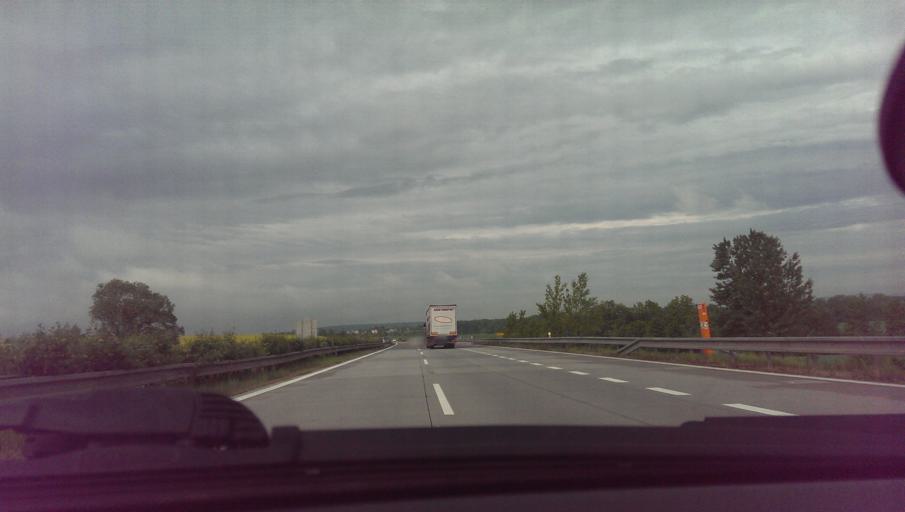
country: CZ
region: South Moravian
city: Ivanovice na Hane
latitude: 49.2890
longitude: 17.0910
